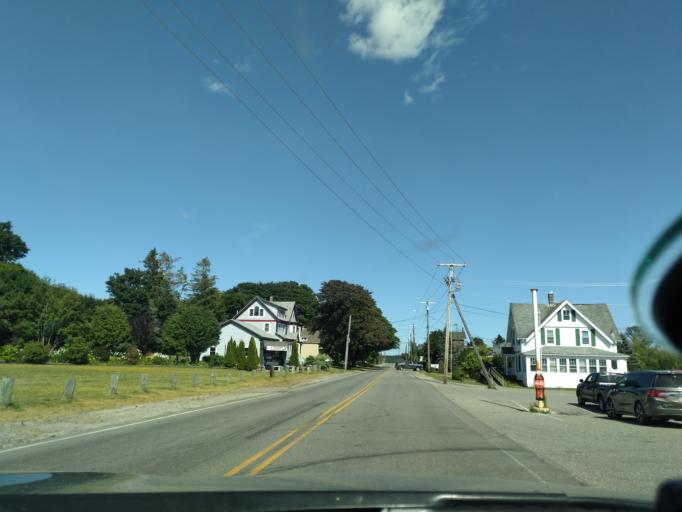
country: US
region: Maine
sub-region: Washington County
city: Eastport
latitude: 44.8578
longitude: -66.9904
